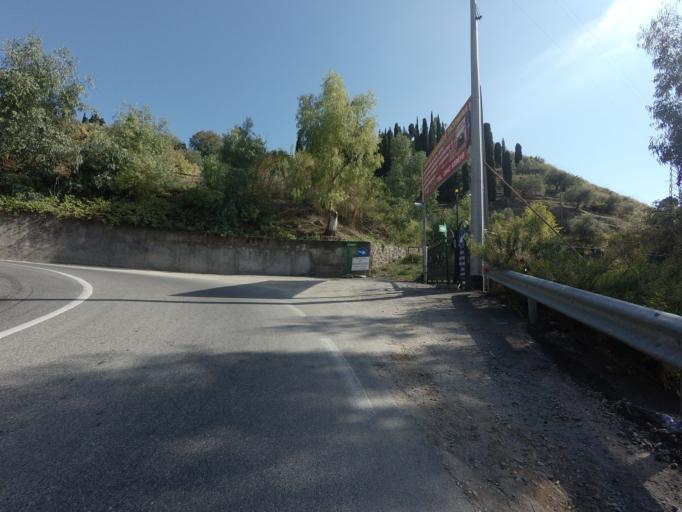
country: IT
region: Sicily
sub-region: Messina
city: Castelmola
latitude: 37.8494
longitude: 15.2789
